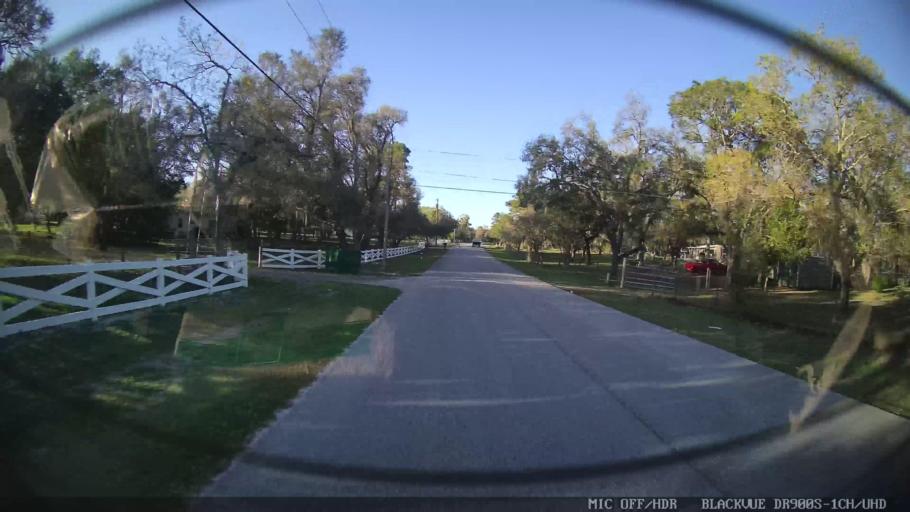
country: US
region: Florida
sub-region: Pasco County
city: Shady Hills
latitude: 28.4112
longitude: -82.5738
